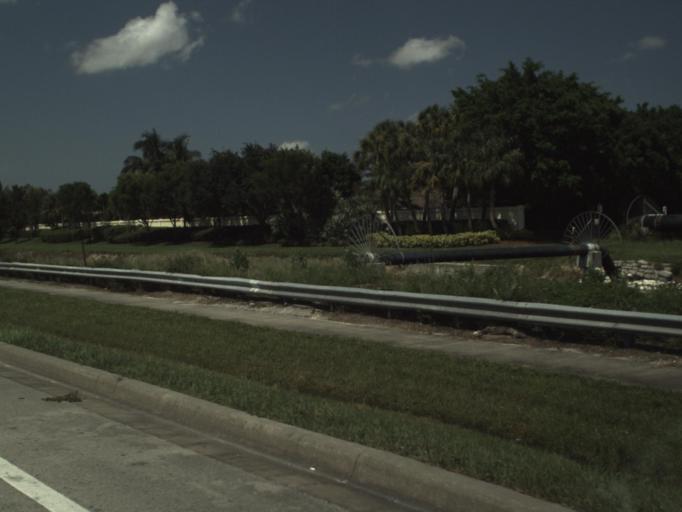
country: US
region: Florida
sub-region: Palm Beach County
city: Wellington
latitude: 26.6540
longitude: -80.2032
